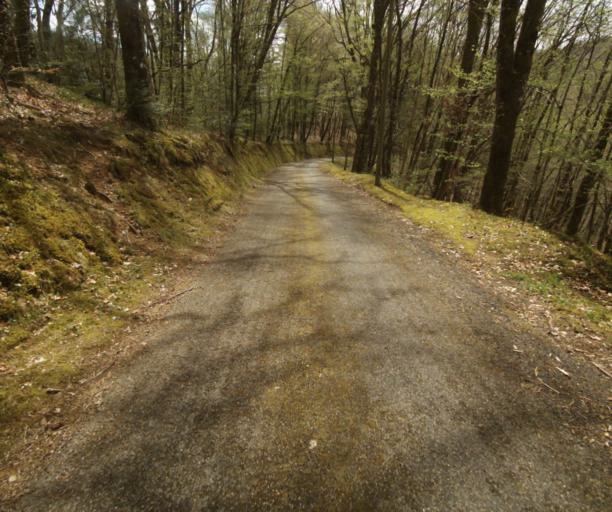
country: FR
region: Limousin
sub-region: Departement de la Correze
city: Sainte-Fortunade
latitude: 45.1908
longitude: 1.8768
